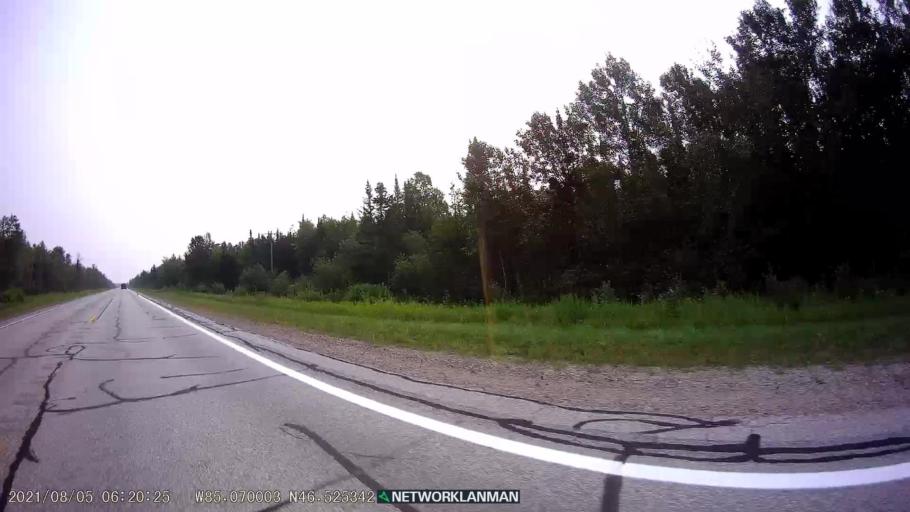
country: US
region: Michigan
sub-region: Luce County
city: Newberry
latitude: 46.5265
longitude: -85.0683
